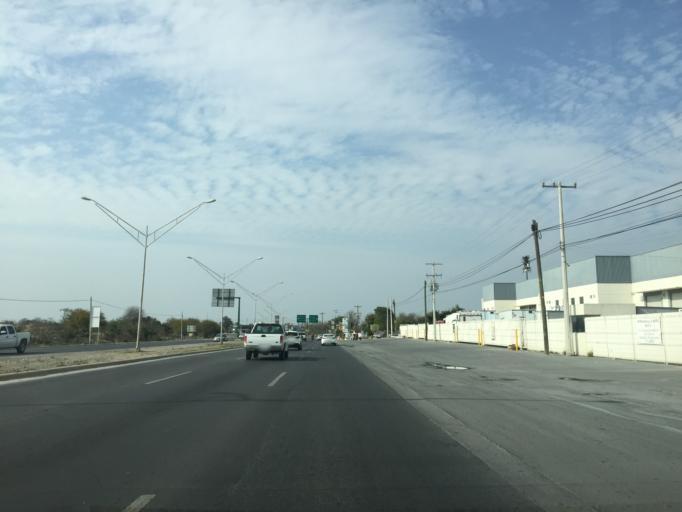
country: MX
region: Nuevo Leon
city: Apodaca
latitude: 25.7697
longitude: -100.1992
